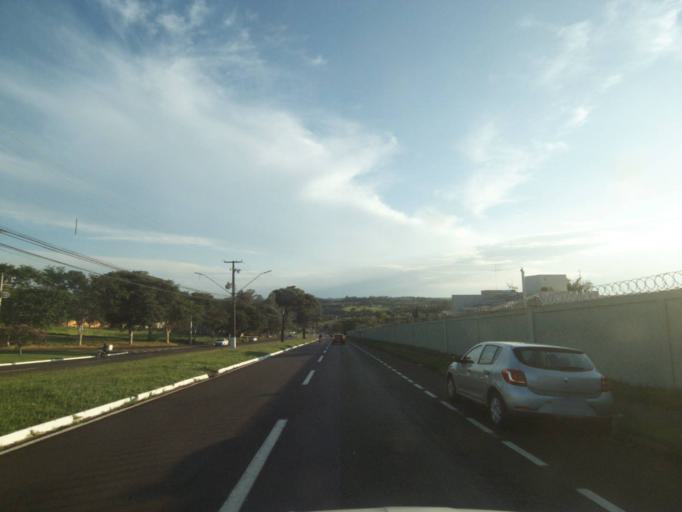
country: BR
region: Parana
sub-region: Londrina
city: Londrina
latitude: -23.3477
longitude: -51.1903
